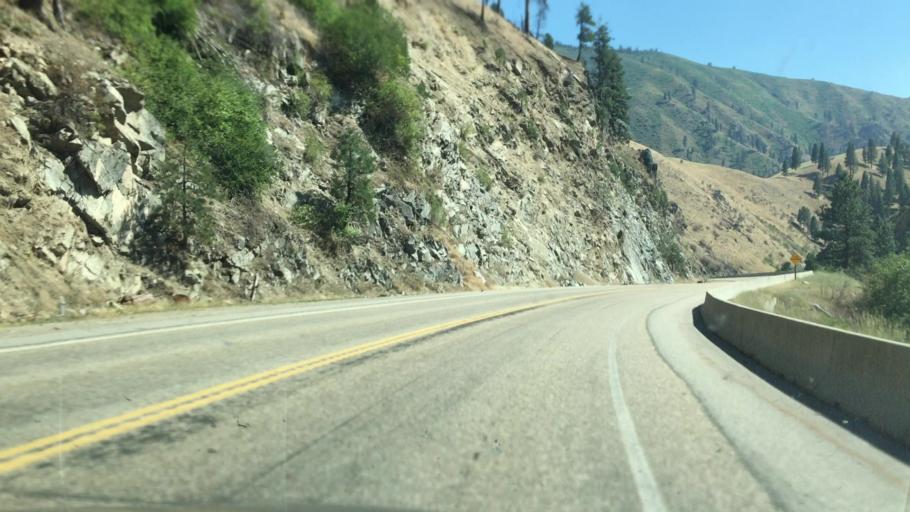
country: US
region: Idaho
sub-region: Boise County
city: Idaho City
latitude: 44.1065
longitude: -116.0951
